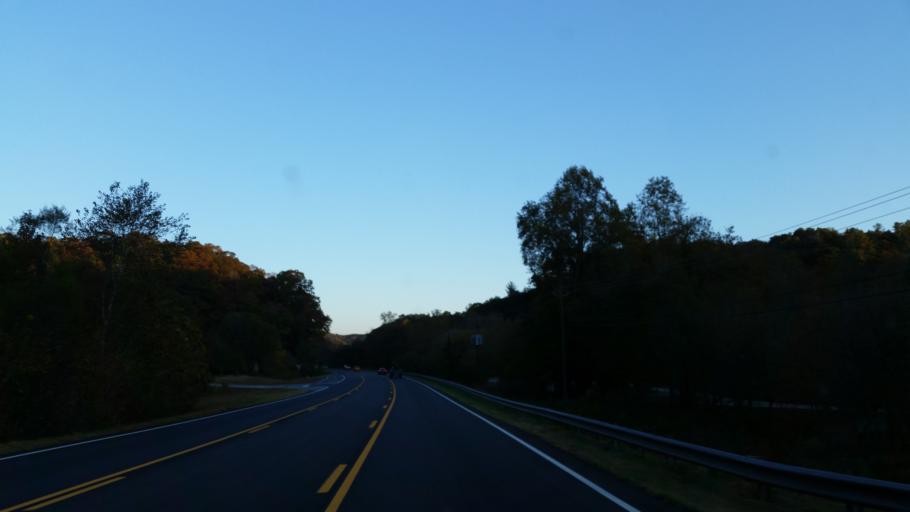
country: US
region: Georgia
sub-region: Lumpkin County
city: Dahlonega
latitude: 34.4719
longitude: -83.9768
